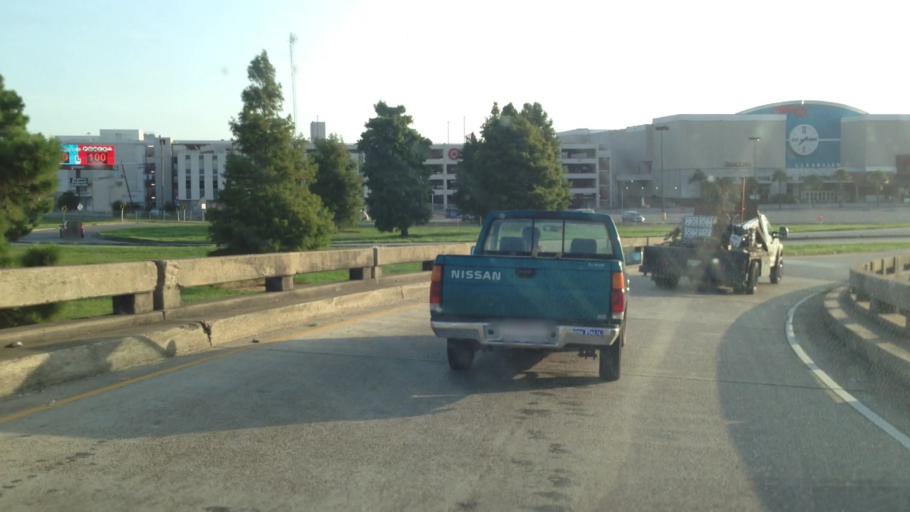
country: US
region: Louisiana
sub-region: Jefferson Parish
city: Metairie Terrace
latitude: 30.0003
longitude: -90.1843
